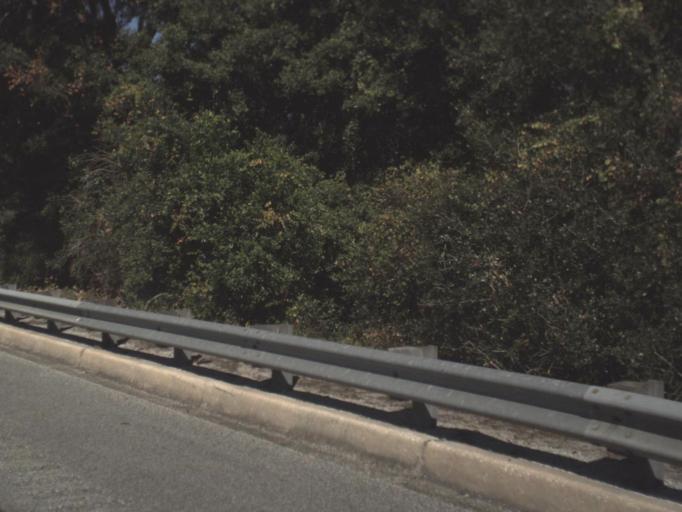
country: US
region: Florida
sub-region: Lake County
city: Howie In The Hills
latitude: 28.6488
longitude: -81.8011
